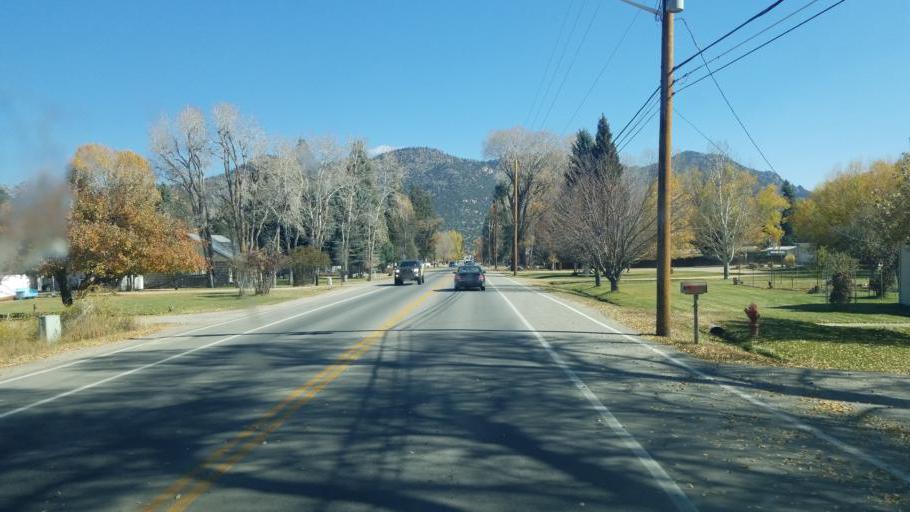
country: US
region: Colorado
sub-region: Chaffee County
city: Buena Vista
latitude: 38.8394
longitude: -106.1406
